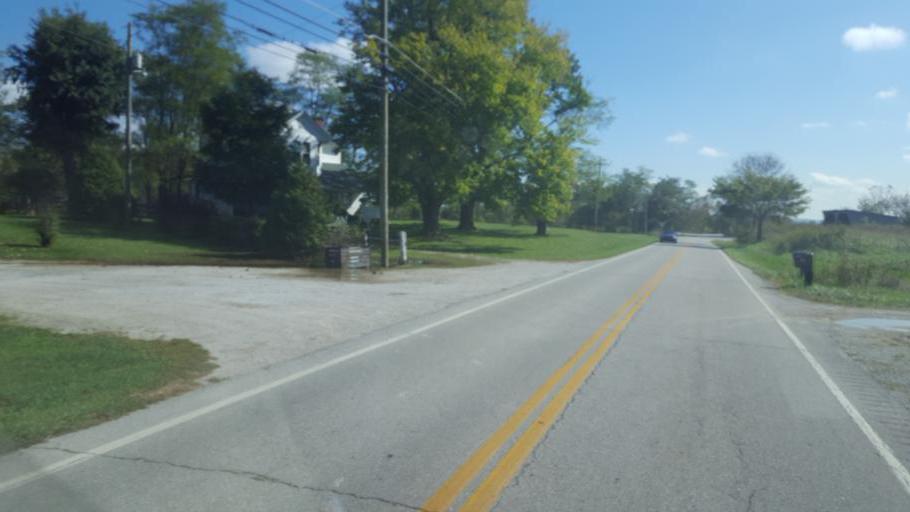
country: US
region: Kentucky
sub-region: Mason County
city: Maysville
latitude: 38.5829
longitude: -83.6514
